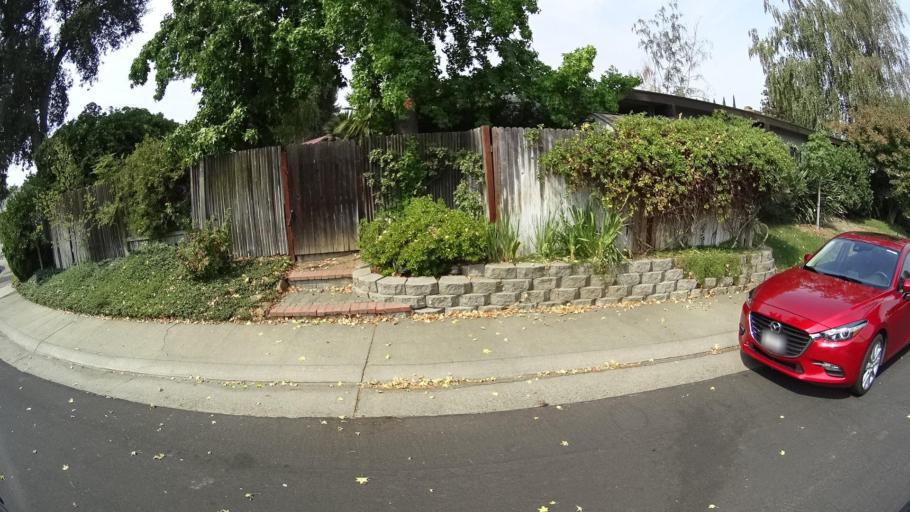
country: US
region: California
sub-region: Sacramento County
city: Elk Grove
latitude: 38.4120
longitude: -121.3785
